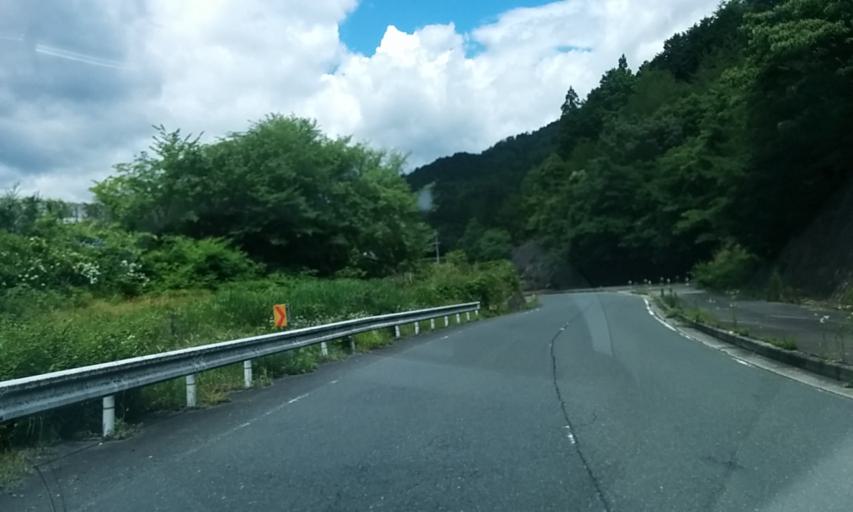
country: JP
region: Kyoto
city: Kameoka
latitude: 35.0105
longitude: 135.4523
